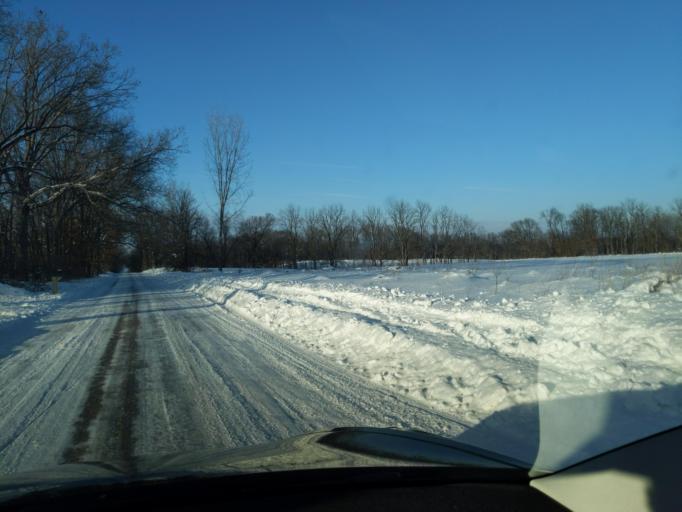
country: US
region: Michigan
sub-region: Ingham County
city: Stockbridge
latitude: 42.4751
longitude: -84.1198
